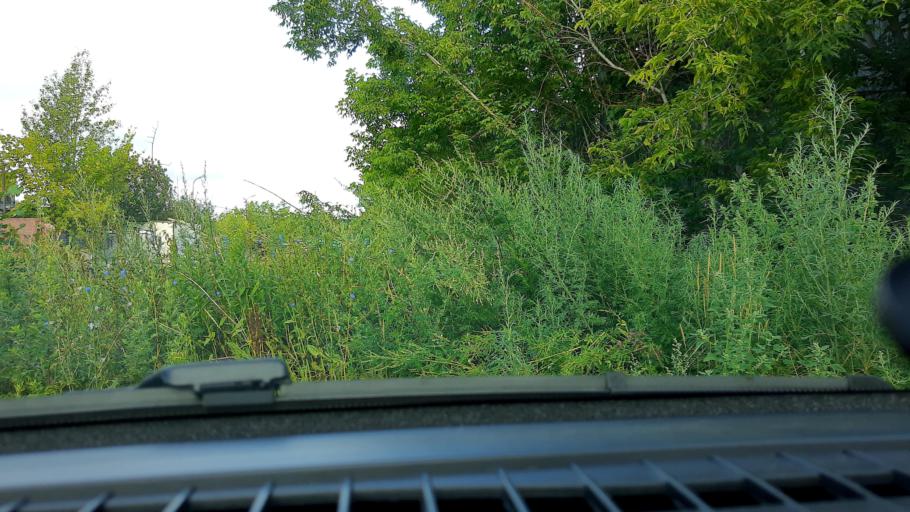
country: RU
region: Nizjnij Novgorod
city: Gorbatovka
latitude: 56.2507
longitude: 43.8312
